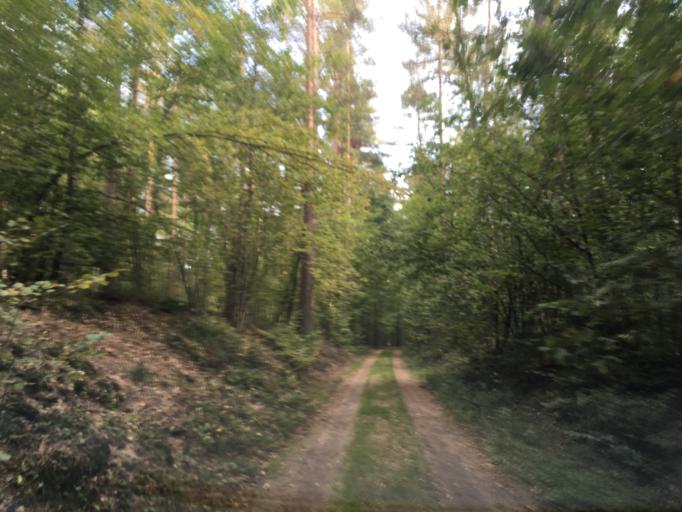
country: PL
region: Kujawsko-Pomorskie
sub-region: Powiat brodnicki
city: Gorzno
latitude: 53.2257
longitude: 19.7128
